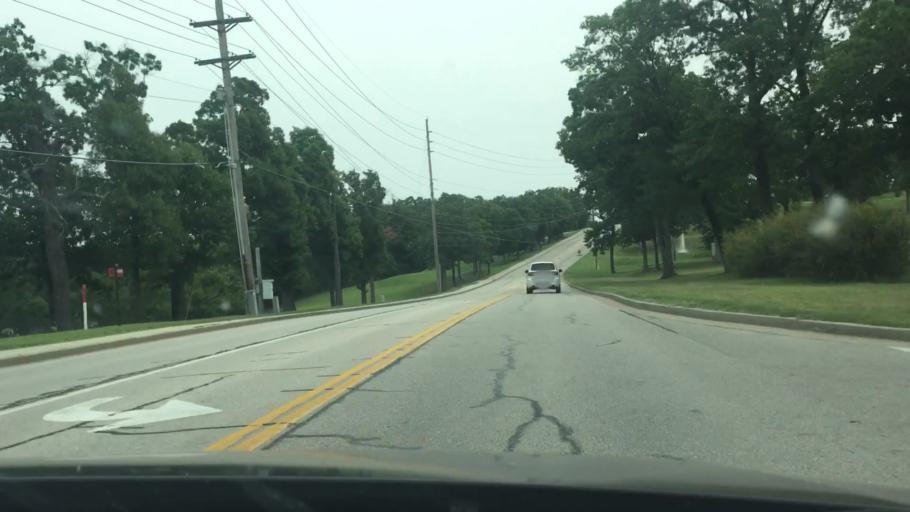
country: US
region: Missouri
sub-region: Camden County
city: Four Seasons
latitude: 38.1914
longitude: -92.6876
